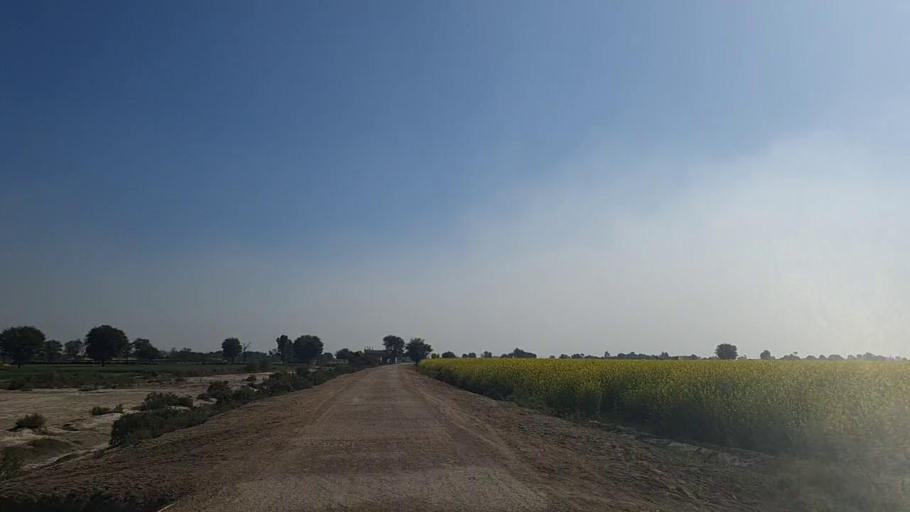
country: PK
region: Sindh
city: Shahpur Chakar
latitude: 26.2044
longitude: 68.6126
